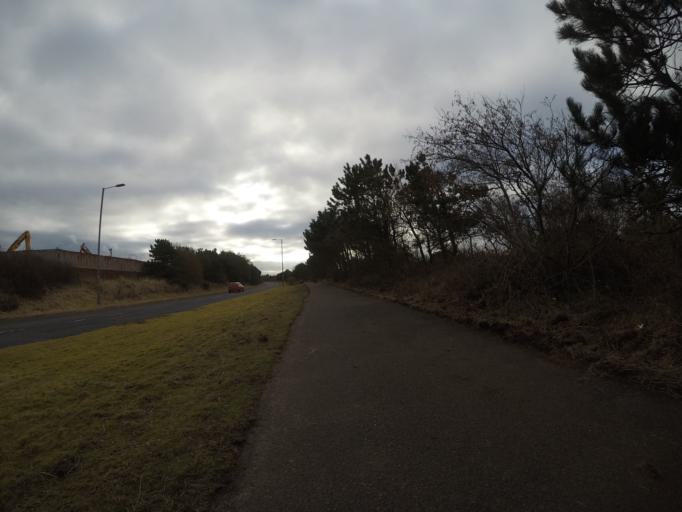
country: GB
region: Scotland
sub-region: North Ayrshire
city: Irvine
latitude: 55.5993
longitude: -4.6784
